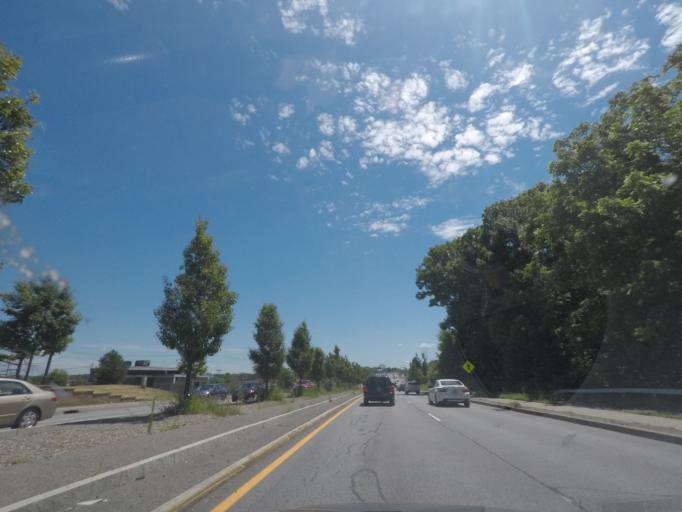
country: US
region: New York
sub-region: Albany County
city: Roessleville
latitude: 42.7554
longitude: -73.7743
